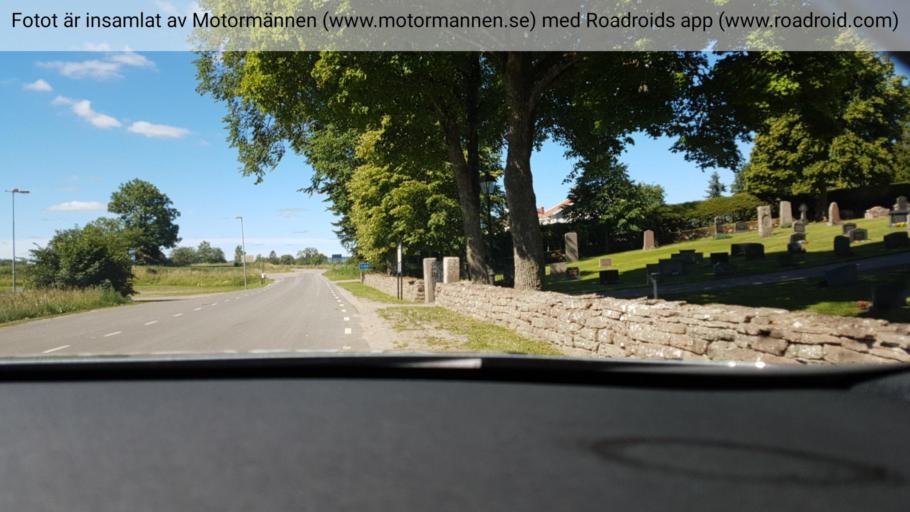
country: SE
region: Vaestra Goetaland
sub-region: Falkopings Kommun
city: Akarp
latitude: 58.1938
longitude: 13.7217
